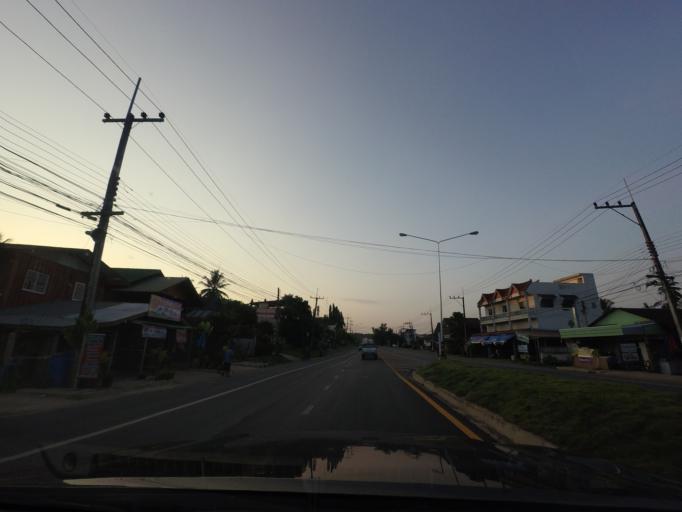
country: TH
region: Nan
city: Na Noi
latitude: 18.3382
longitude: 100.7153
